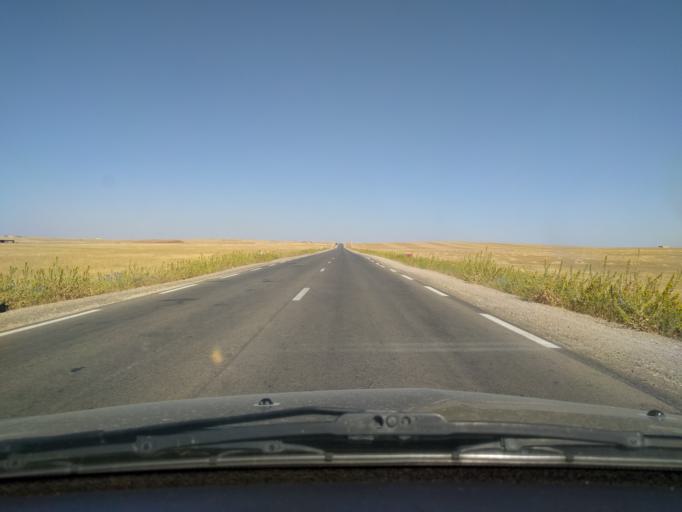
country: DZ
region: Tiaret
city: Frenda
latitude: 34.8808
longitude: 1.1947
